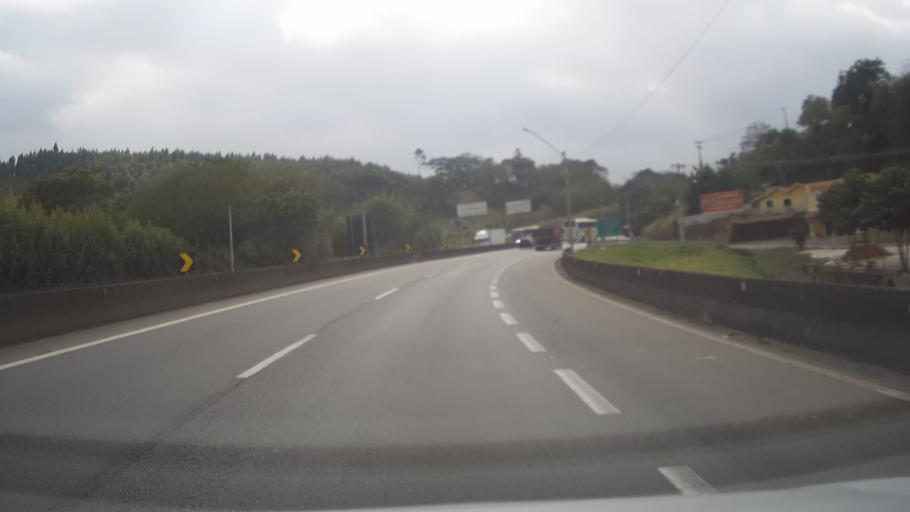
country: BR
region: Minas Gerais
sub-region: Extrema
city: Extrema
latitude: -22.8784
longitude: -46.3981
